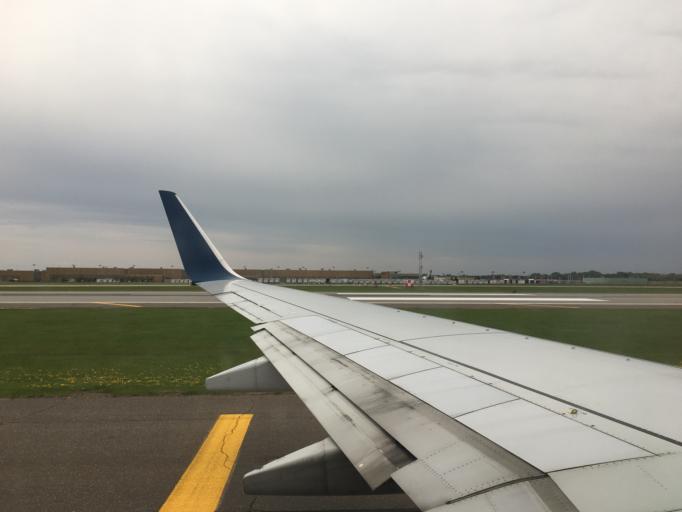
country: US
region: Minnesota
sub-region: Hennepin County
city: Richfield
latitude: 44.8870
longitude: -93.2292
